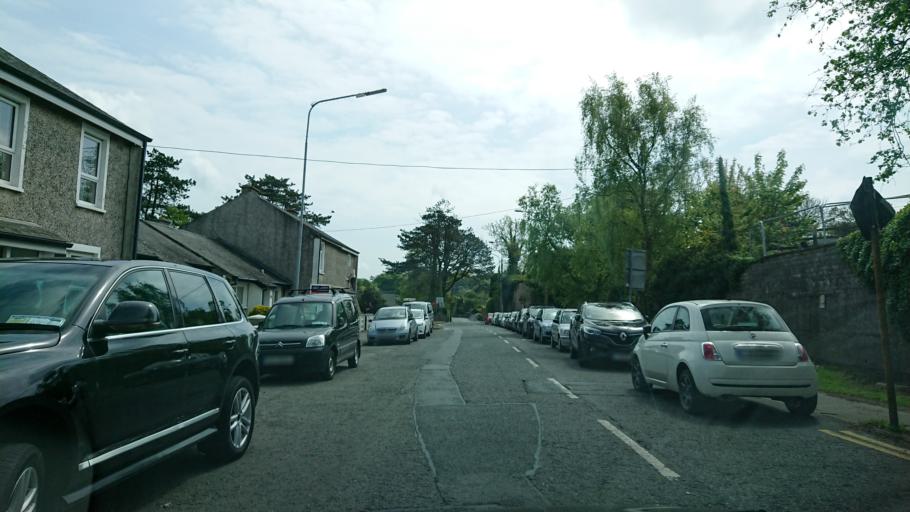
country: IE
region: Munster
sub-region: Waterford
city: Waterford
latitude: 52.2511
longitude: -7.1032
